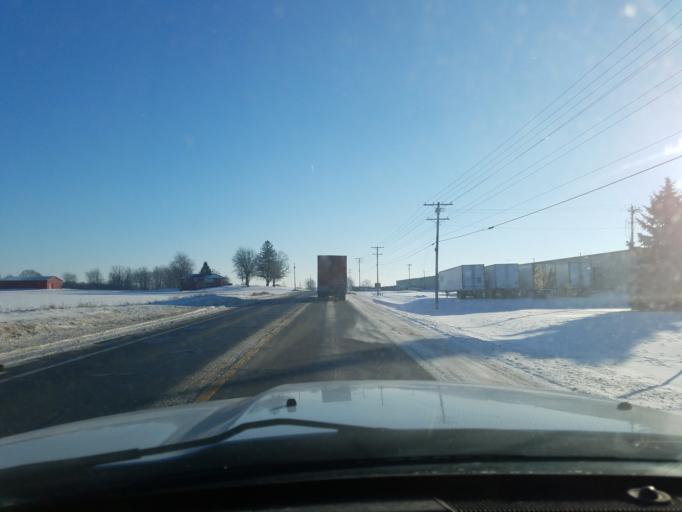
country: US
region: Indiana
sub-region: Noble County
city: Rome City
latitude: 41.4526
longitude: -85.3439
